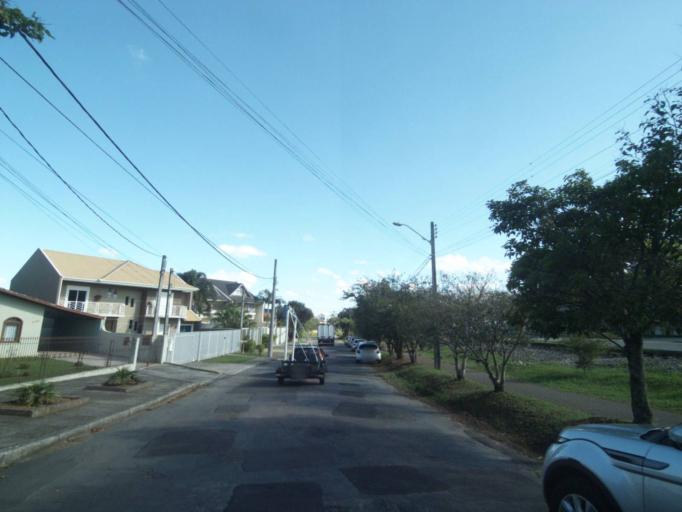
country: BR
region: Parana
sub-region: Curitiba
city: Curitiba
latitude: -25.3912
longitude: -49.2579
